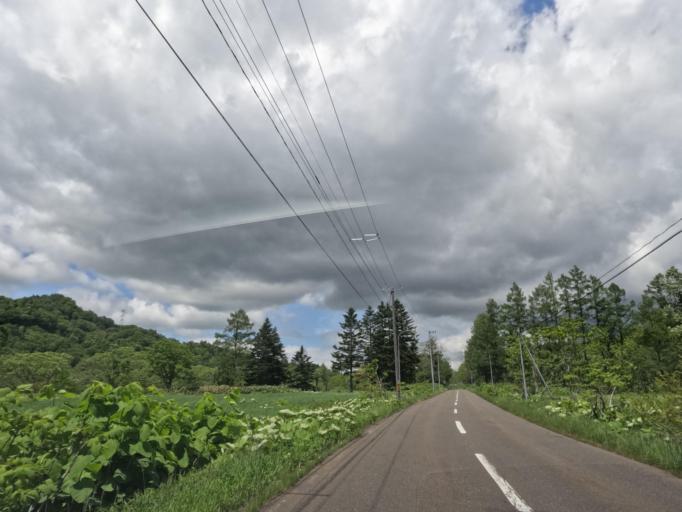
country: JP
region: Hokkaido
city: Tobetsu
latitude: 43.4397
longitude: 141.5823
